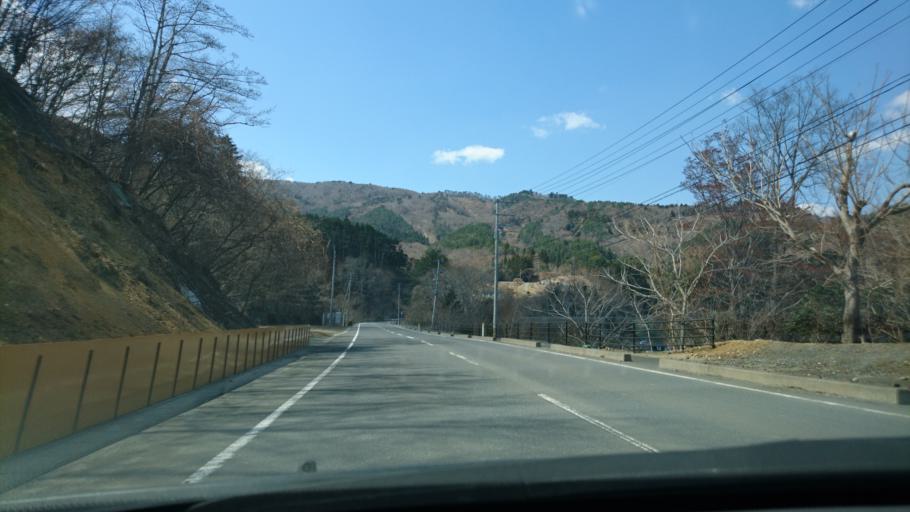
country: JP
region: Miyagi
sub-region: Oshika Gun
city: Onagawa Cho
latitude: 38.4866
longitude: 141.4907
